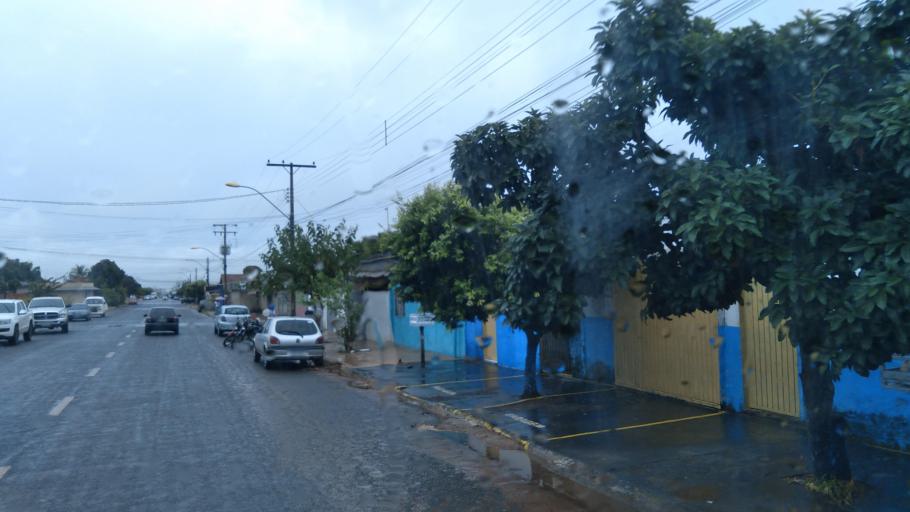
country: BR
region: Goias
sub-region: Mineiros
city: Mineiros
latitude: -17.5391
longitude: -52.5409
